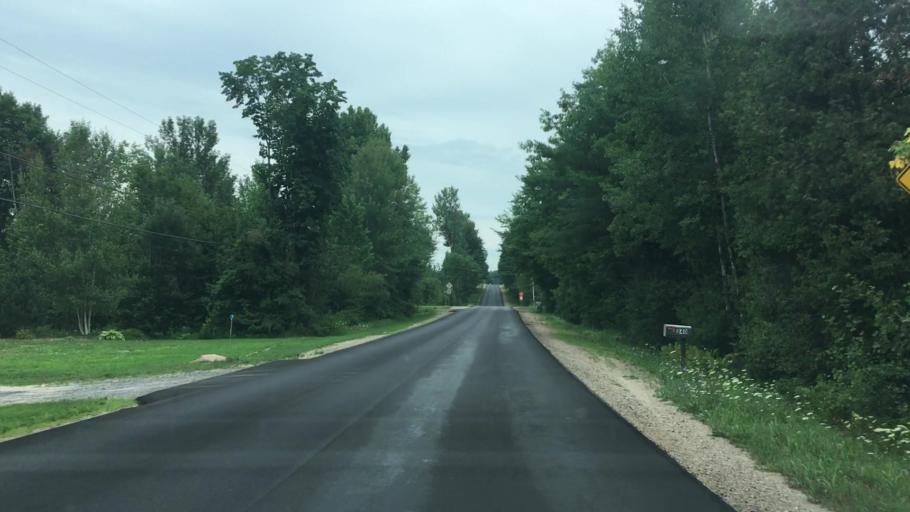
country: US
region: New York
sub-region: Clinton County
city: Peru
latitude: 44.5772
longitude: -73.5699
